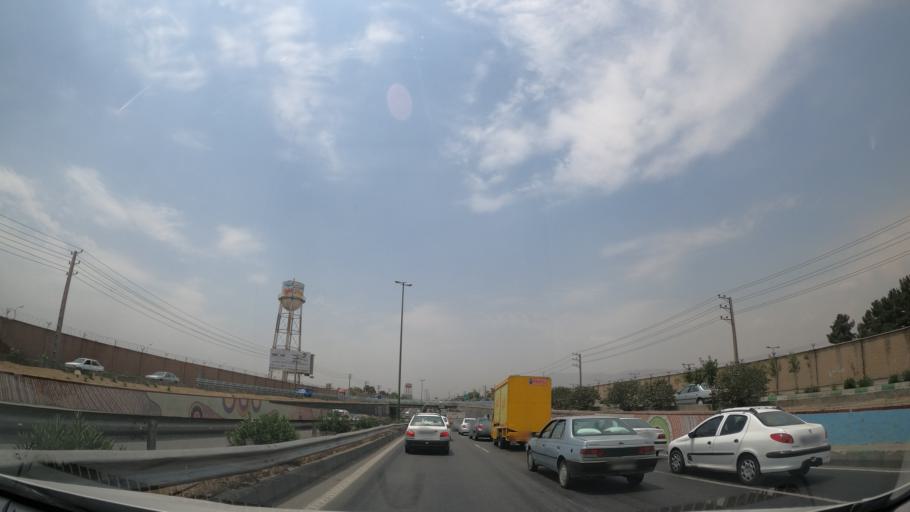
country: IR
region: Tehran
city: Shahr-e Qods
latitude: 35.6912
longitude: 51.2139
